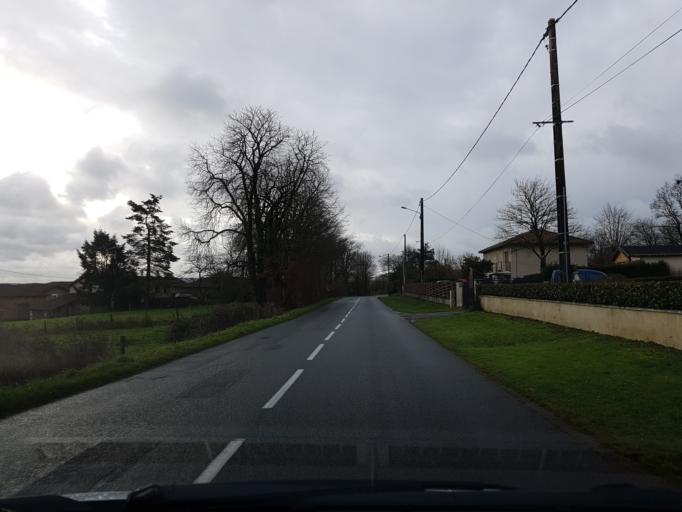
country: FR
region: Poitou-Charentes
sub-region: Departement de la Charente
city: Chabanais
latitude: 45.8974
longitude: 0.7307
